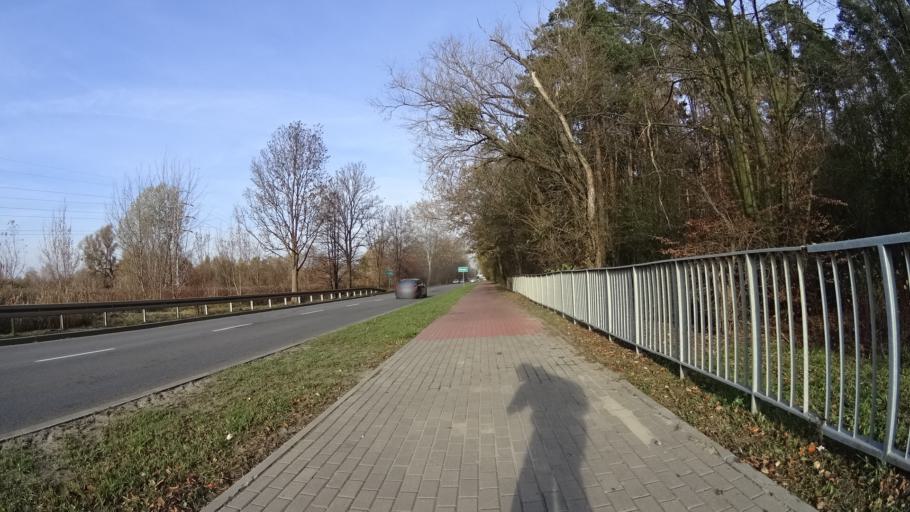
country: PL
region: Masovian Voivodeship
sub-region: Powiat warszawski zachodni
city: Babice
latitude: 52.2685
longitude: 20.8601
